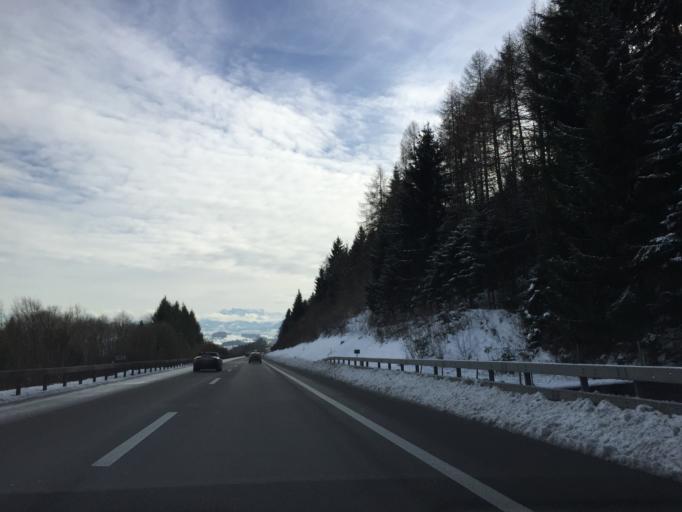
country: CH
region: Zurich
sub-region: Bezirk Horgen
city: Horgen / Oberdorf
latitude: 47.2553
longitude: 8.5872
